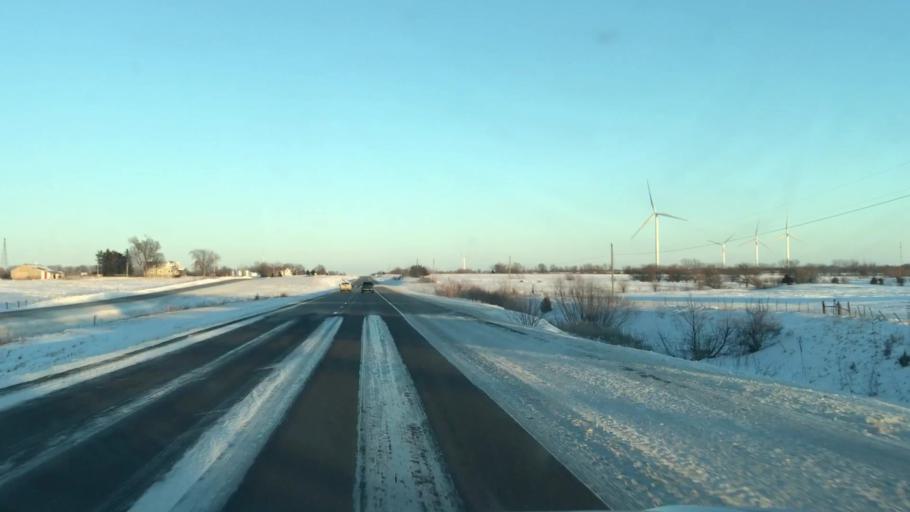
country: US
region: Missouri
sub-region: DeKalb County
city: Maysville
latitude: 39.7616
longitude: -94.4210
